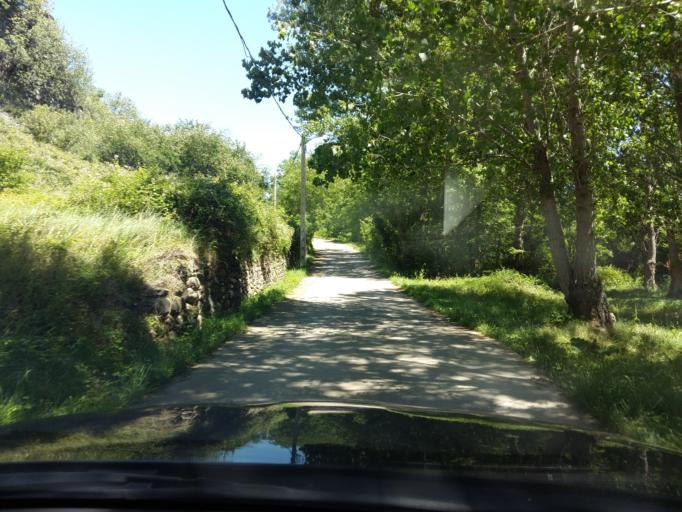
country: ES
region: Aragon
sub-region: Provincia de Zaragoza
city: Alcala de Moncayo
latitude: 41.7765
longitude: -1.7260
